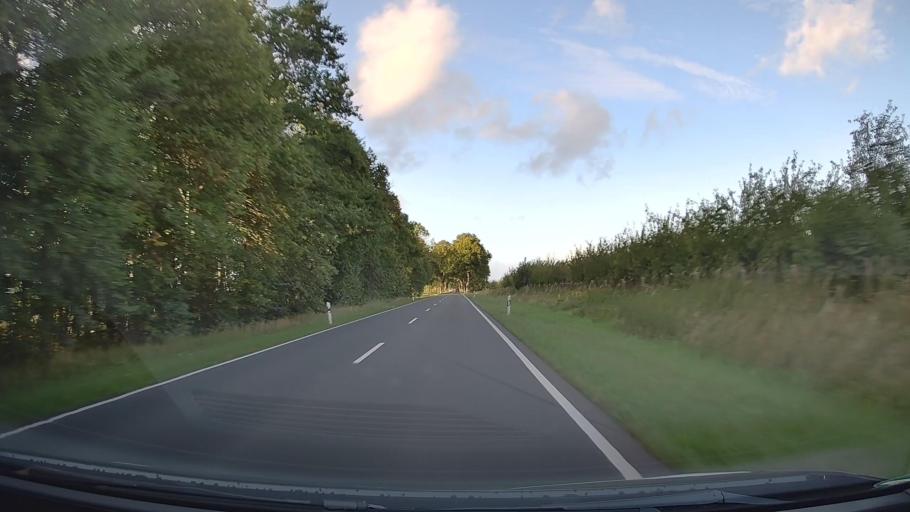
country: DE
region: Mecklenburg-Vorpommern
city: Wendorf
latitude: 54.2661
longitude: 13.0340
